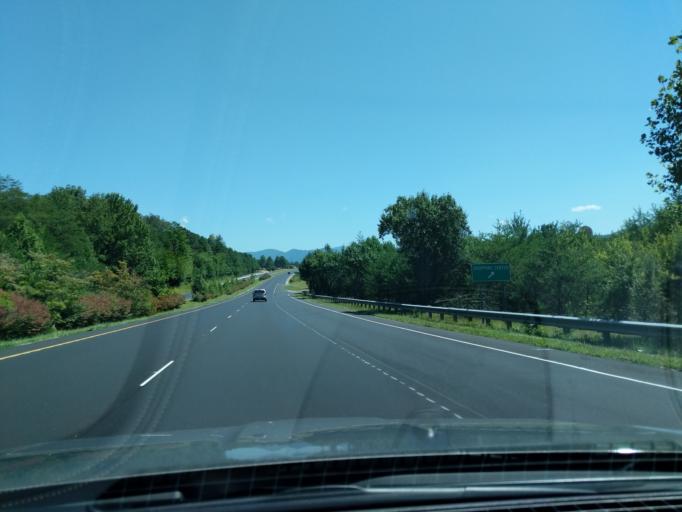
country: US
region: North Carolina
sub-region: Macon County
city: Franklin
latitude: 35.1666
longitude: -83.4023
